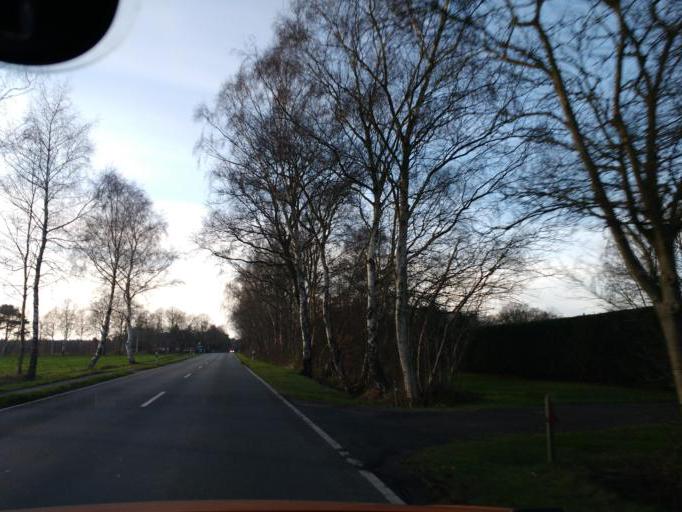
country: DE
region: Lower Saxony
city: Hude
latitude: 53.1019
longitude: 8.4254
